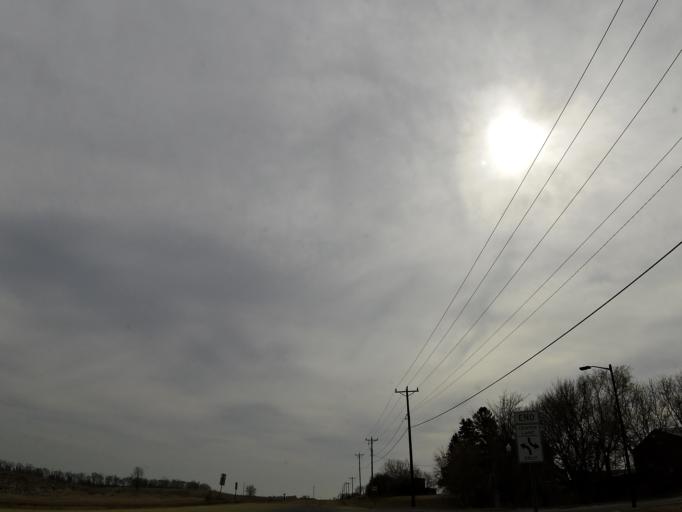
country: US
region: Minnesota
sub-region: Dakota County
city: Rosemount
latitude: 44.7289
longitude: -93.1164
